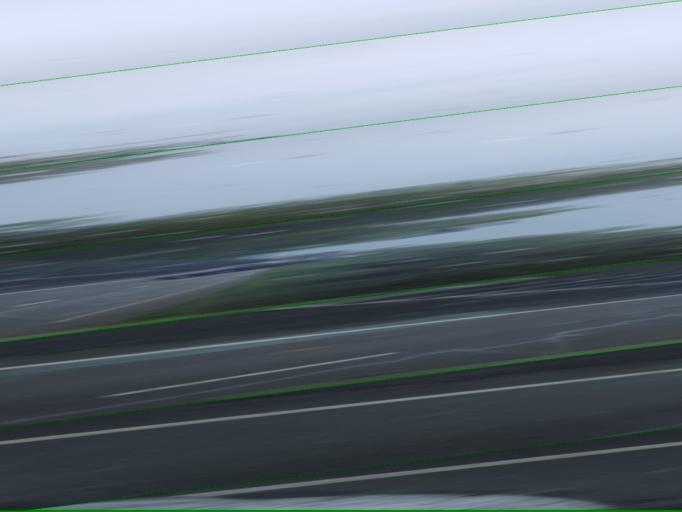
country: FR
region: Centre
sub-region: Departement d'Eure-et-Loir
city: Cherisy
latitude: 48.7494
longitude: 1.4325
